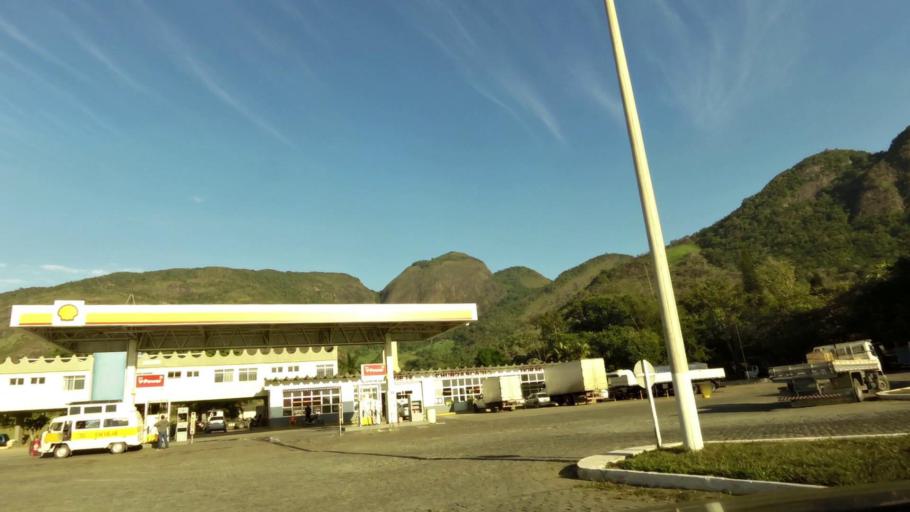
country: BR
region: Espirito Santo
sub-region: Guarapari
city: Guarapari
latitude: -20.5997
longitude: -40.5028
